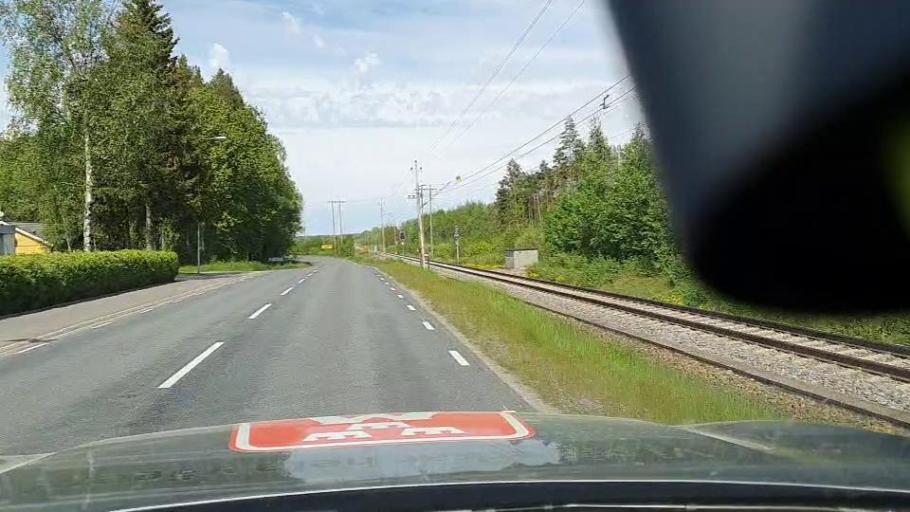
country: SE
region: Soedermanland
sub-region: Eskilstuna Kommun
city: Skogstorp
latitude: 59.2998
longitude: 16.4602
